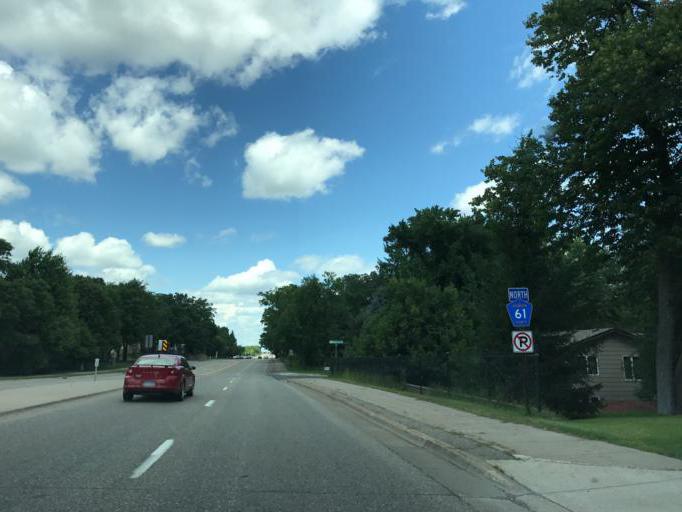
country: US
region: Minnesota
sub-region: Hennepin County
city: Maple Grove
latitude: 45.0731
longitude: -93.4311
